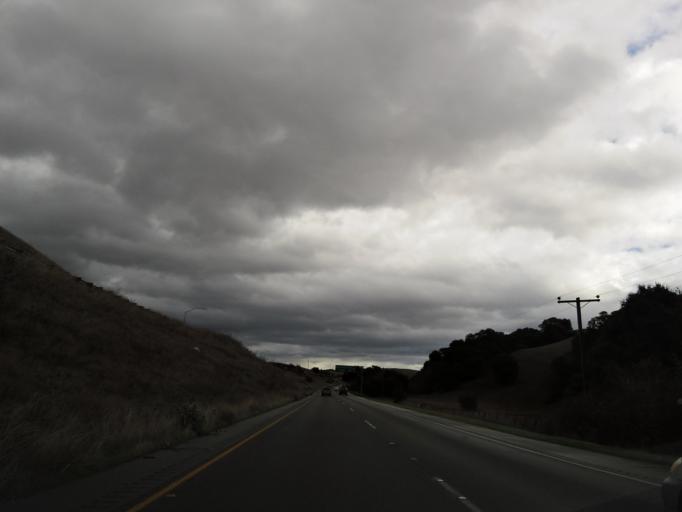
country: US
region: California
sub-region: San Benito County
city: San Juan Bautista
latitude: 36.8607
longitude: -121.5882
